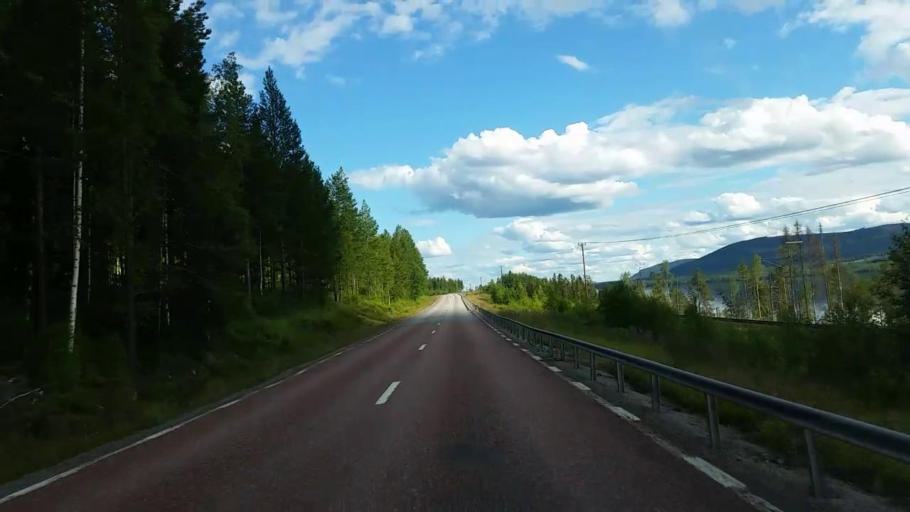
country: SE
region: Gaevleborg
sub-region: Ljusdals Kommun
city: Farila
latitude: 62.1065
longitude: 15.7725
